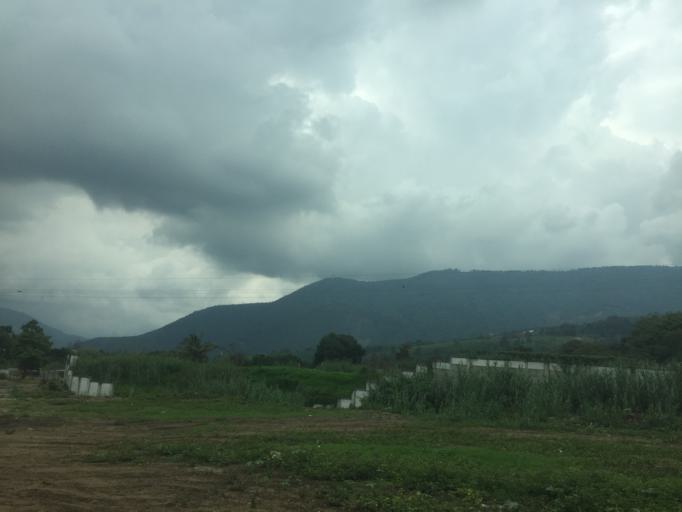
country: GT
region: Guatemala
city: Amatitlan
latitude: 14.4887
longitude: -90.6370
